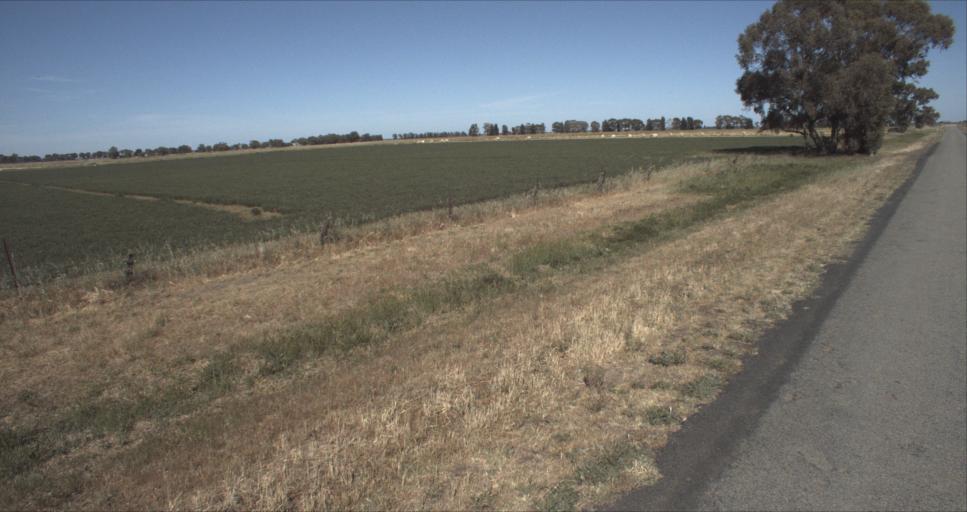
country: AU
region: New South Wales
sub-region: Leeton
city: Leeton
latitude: -34.5337
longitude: 146.3234
